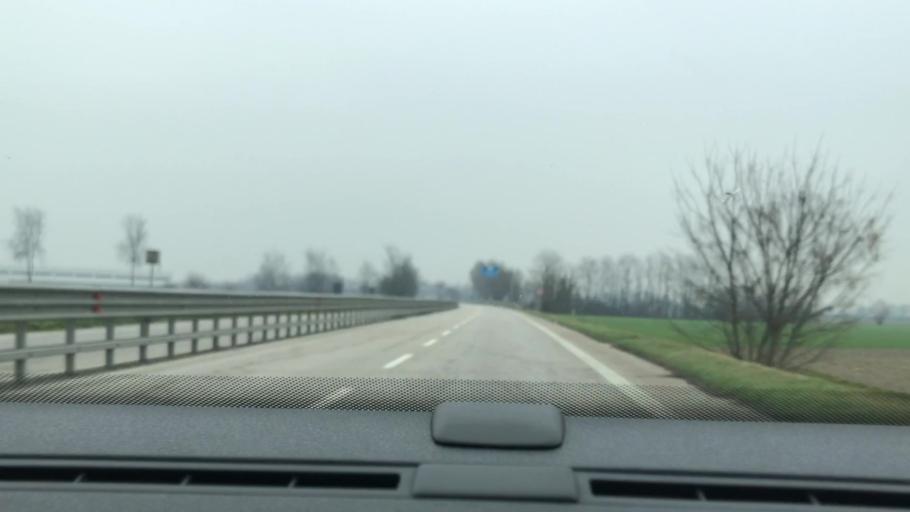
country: IT
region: Veneto
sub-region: Provincia di Rovigo
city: Grignano Polesine
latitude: 45.0253
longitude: 11.7651
